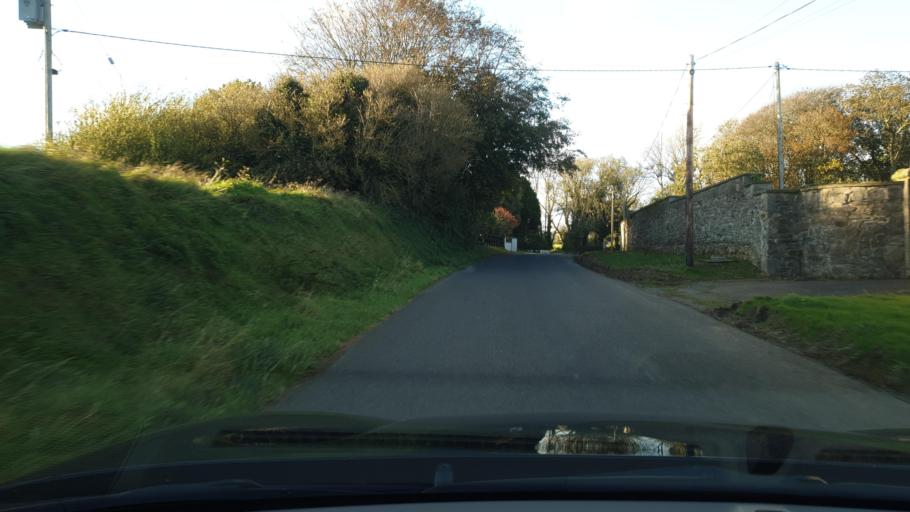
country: IE
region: Leinster
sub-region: An Mhi
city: Stamullin
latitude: 53.6376
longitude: -6.2902
